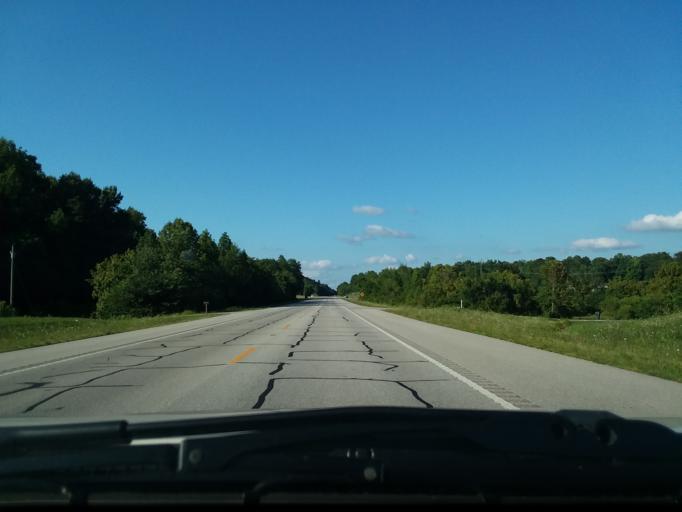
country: US
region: Tennessee
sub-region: Clay County
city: Celina
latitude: 36.6067
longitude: -85.4265
